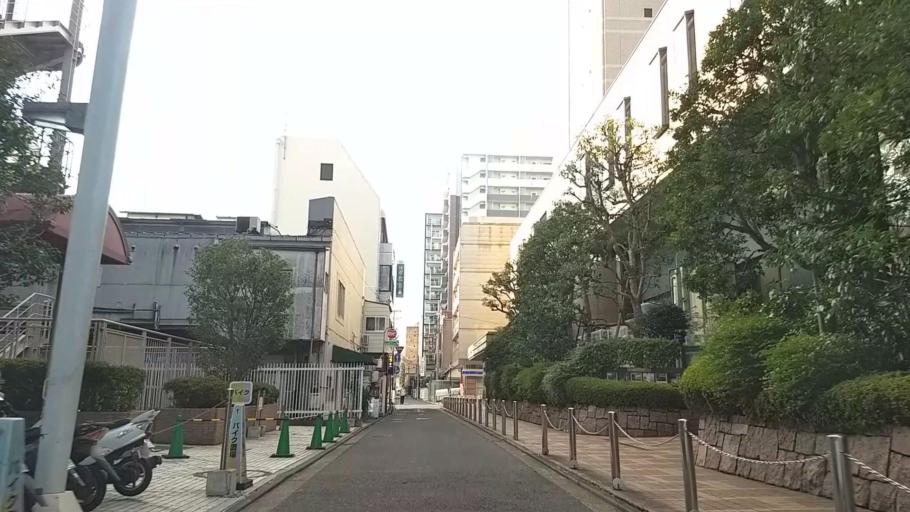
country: JP
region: Kanagawa
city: Atsugi
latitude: 35.4426
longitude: 139.3656
